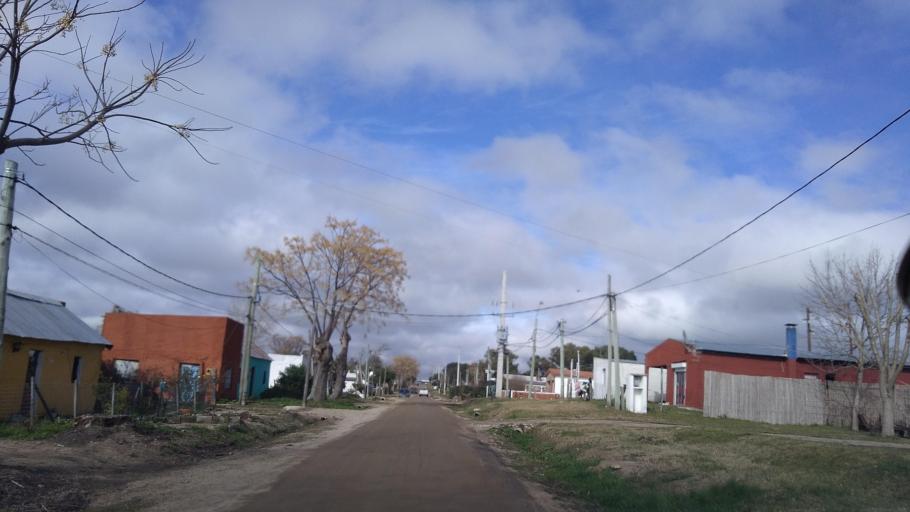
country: UY
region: Canelones
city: Tala
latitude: -34.1911
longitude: -55.7419
